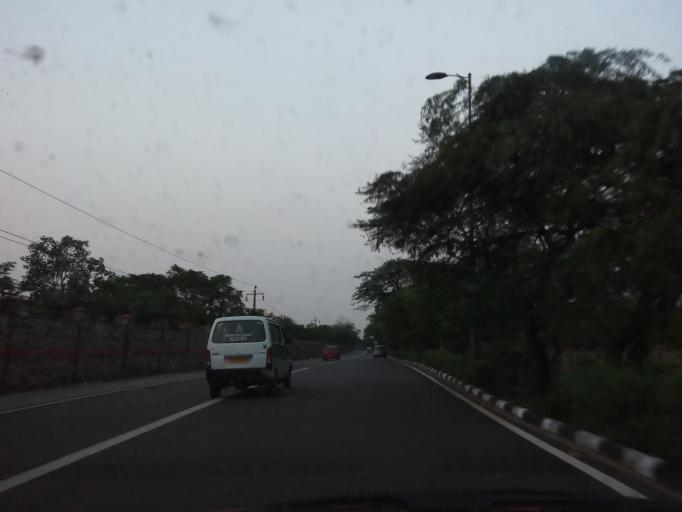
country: IN
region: NCT
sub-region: Central Delhi
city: Karol Bagh
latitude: 28.6315
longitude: 77.1884
